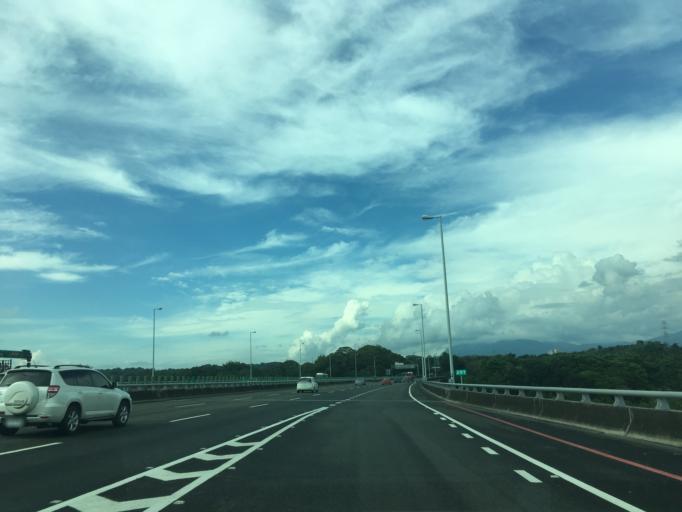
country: TW
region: Taiwan
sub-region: Chiayi
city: Jiayi Shi
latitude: 23.4541
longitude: 120.4873
